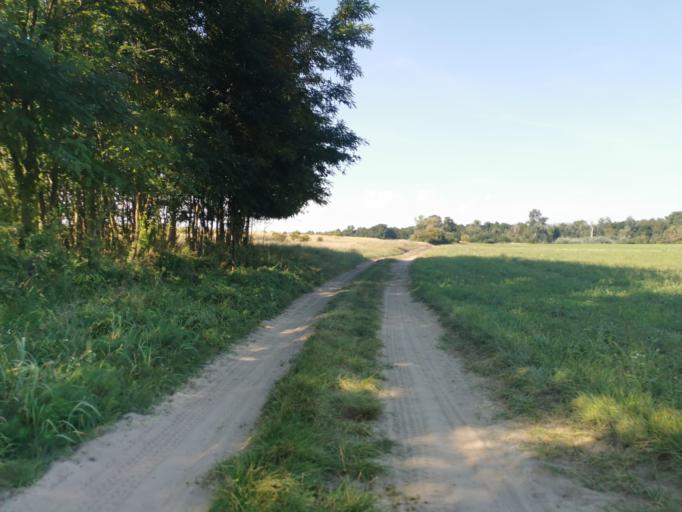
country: SK
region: Trnavsky
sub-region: Okres Senica
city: Senica
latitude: 48.6214
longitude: 17.2320
